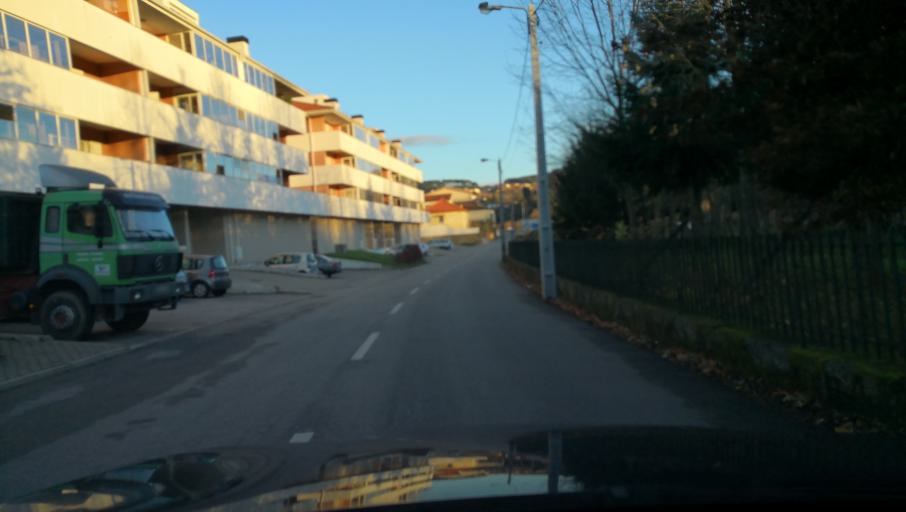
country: PT
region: Vila Real
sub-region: Vila Real
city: Vila Real
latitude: 41.2913
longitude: -7.7270
